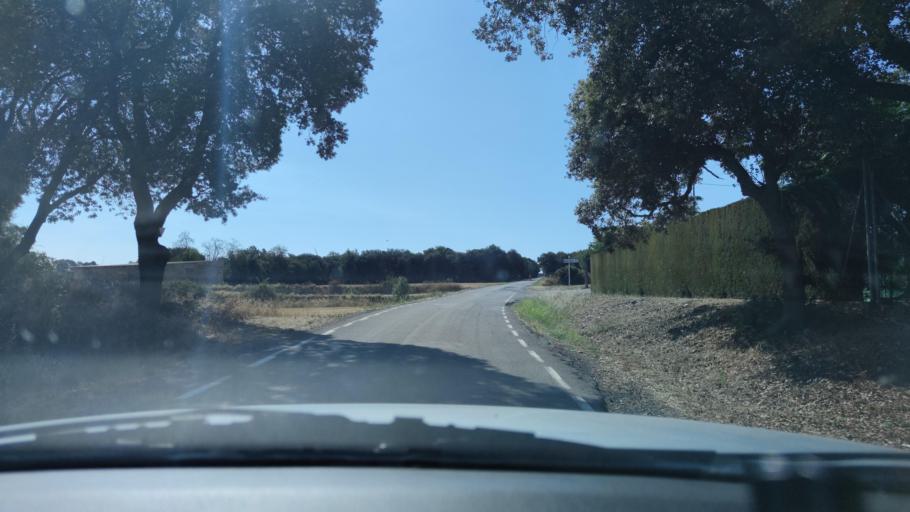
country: ES
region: Catalonia
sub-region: Provincia de Lleida
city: Sant Guim de Freixenet
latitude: 41.6666
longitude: 1.4138
